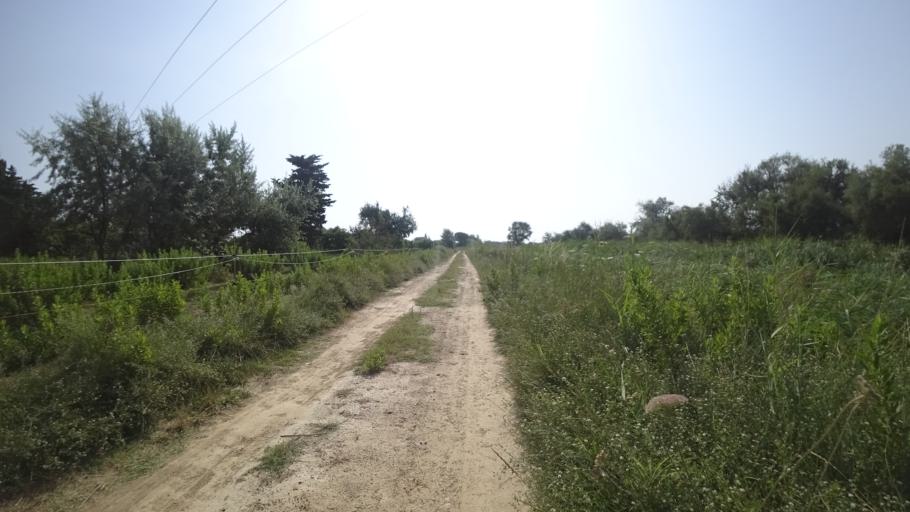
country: FR
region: Languedoc-Roussillon
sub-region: Departement des Pyrenees-Orientales
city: Sainte-Marie-Plage
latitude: 42.7407
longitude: 3.0171
